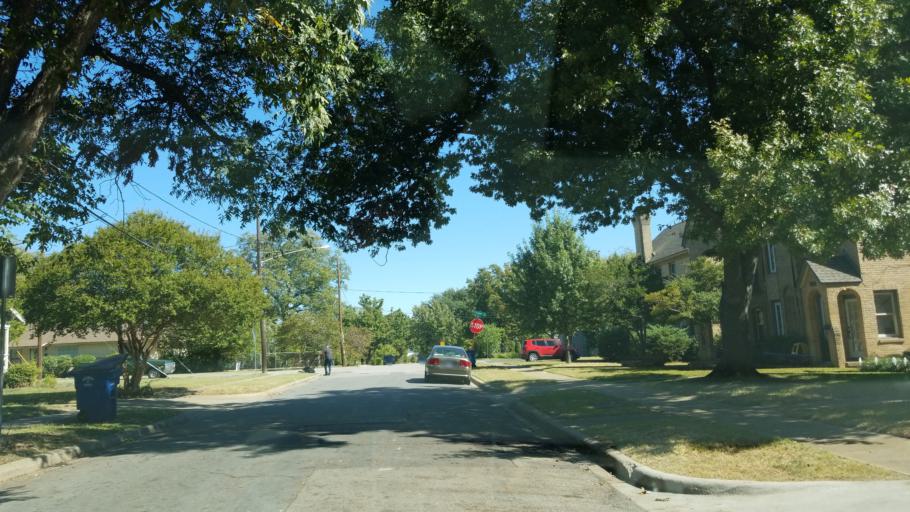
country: US
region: Texas
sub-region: Dallas County
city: Highland Park
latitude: 32.8083
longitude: -96.7511
